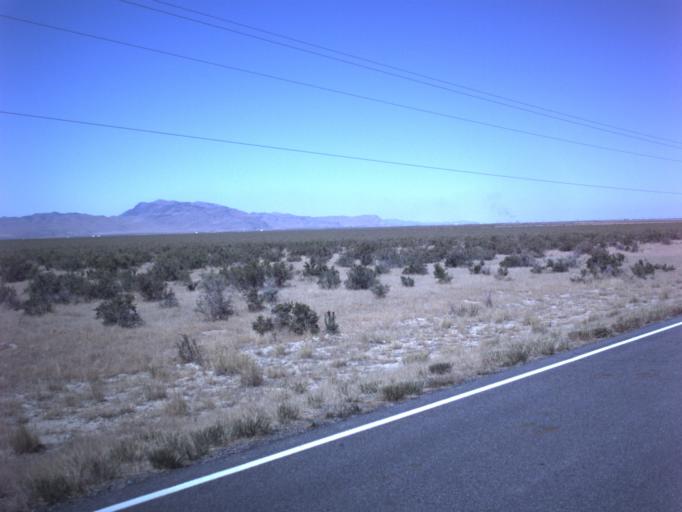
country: US
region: Utah
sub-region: Tooele County
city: Grantsville
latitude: 40.7077
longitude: -112.6637
